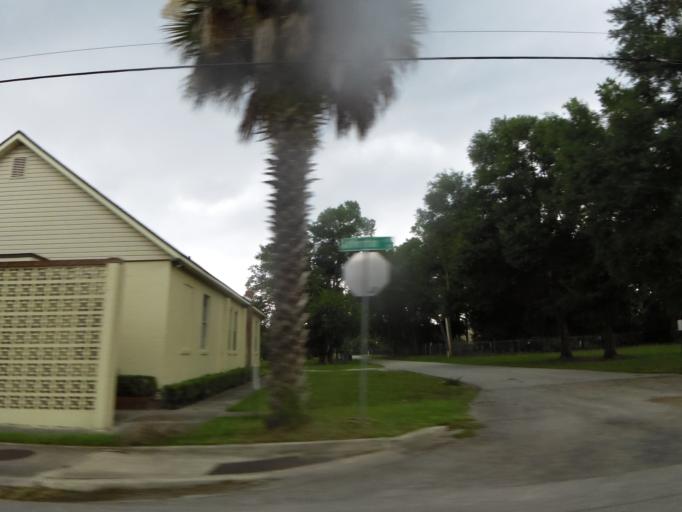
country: US
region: Florida
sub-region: Duval County
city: Jacksonville
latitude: 30.3336
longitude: -81.5947
